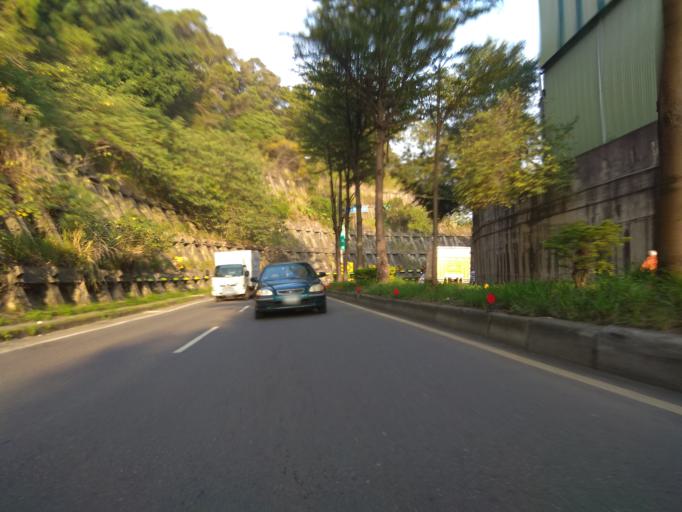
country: TW
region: Taiwan
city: Daxi
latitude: 24.9239
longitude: 121.1863
